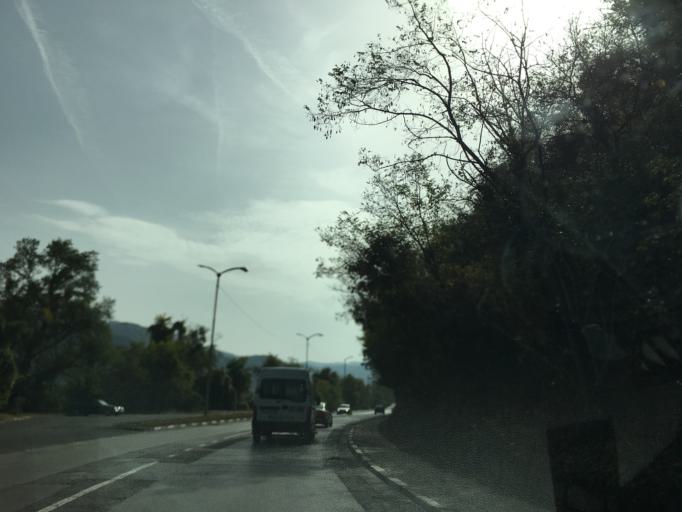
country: BG
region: Sofia-Capital
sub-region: Stolichna Obshtina
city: Sofia
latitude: 42.5927
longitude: 23.4172
